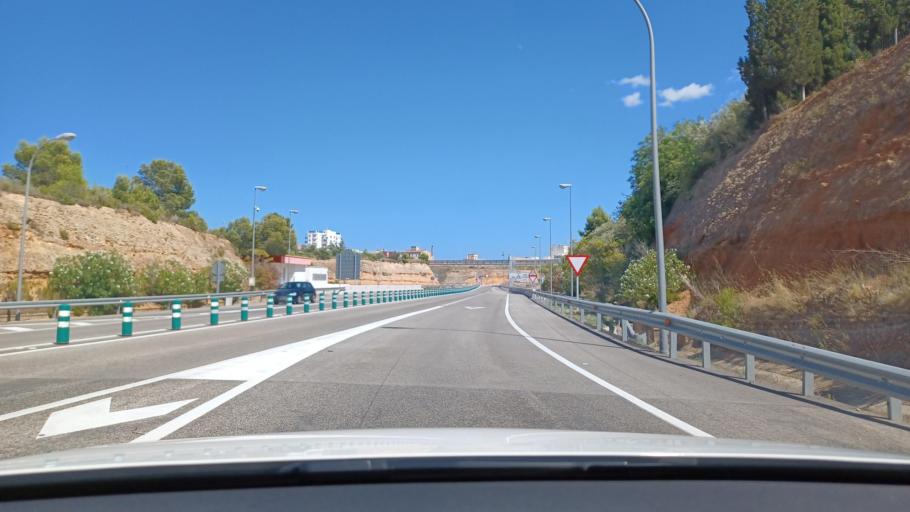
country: ES
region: Catalonia
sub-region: Provincia de Tarragona
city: L'Ampolla
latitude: 40.8114
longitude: 0.7021
